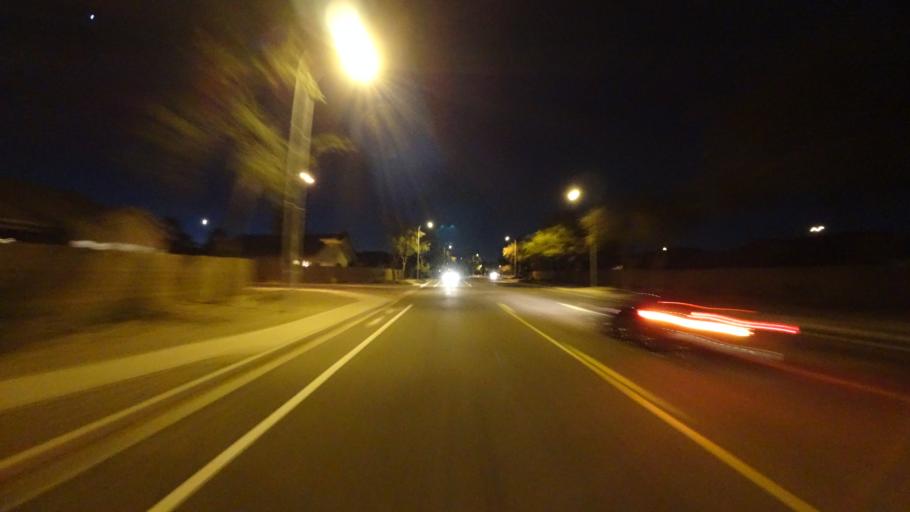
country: US
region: Arizona
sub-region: Maricopa County
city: Sun Lakes
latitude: 33.2517
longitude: -111.8528
